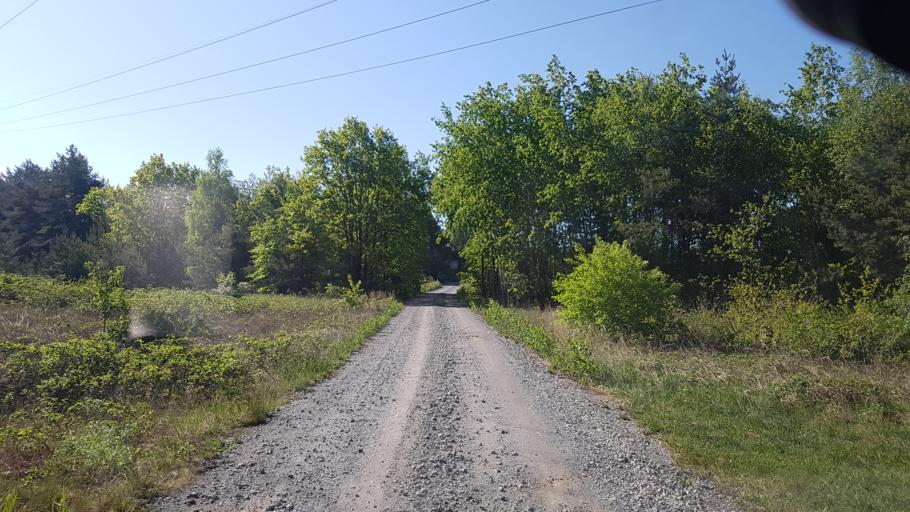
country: DE
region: Brandenburg
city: Grossraschen
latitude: 51.5900
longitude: 13.9612
